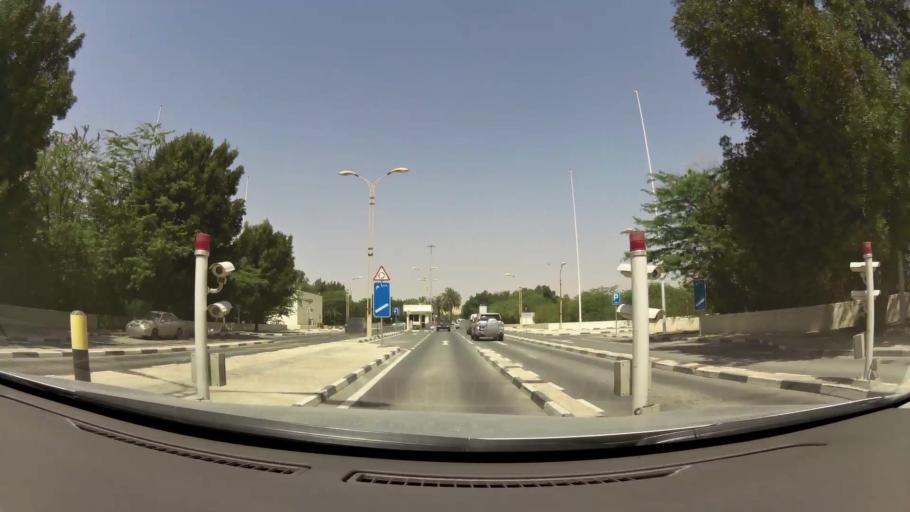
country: QA
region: Baladiyat ad Dawhah
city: Doha
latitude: 25.3683
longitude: 51.4947
